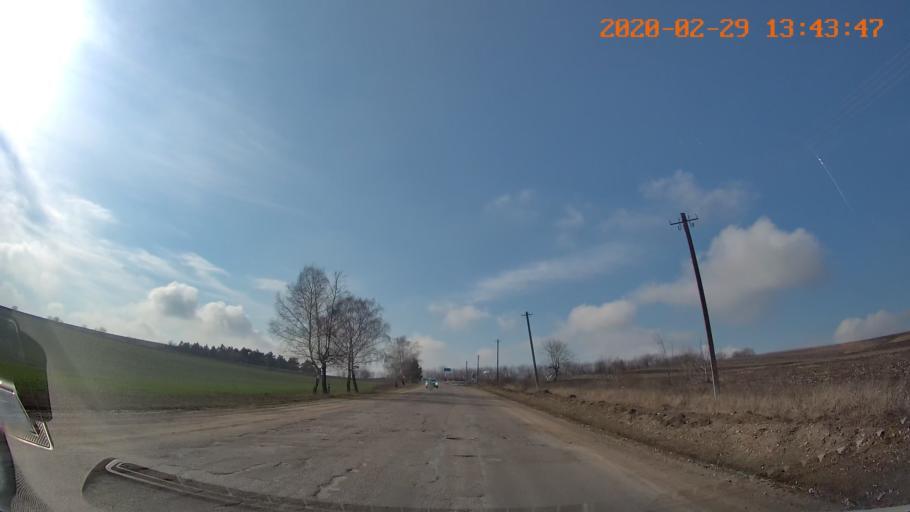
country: MD
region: Floresti
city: Leninskiy
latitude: 47.8392
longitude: 28.5275
